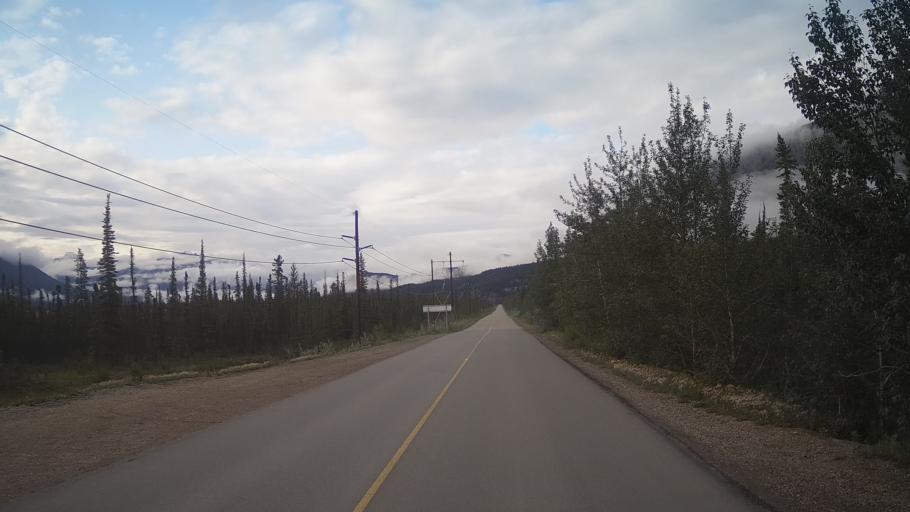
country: CA
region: Alberta
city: Jasper Park Lodge
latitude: 53.0091
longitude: -118.0862
